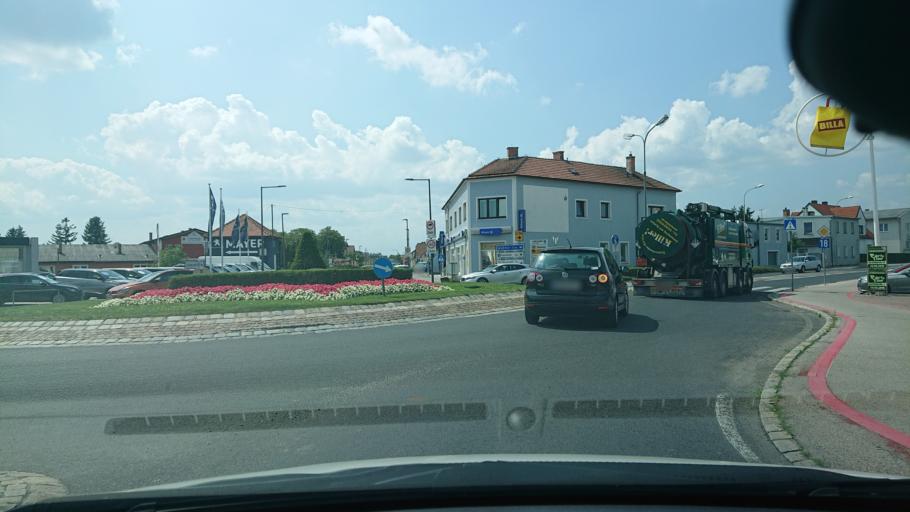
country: AT
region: Lower Austria
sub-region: Politischer Bezirk Baden
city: Leobersdorf
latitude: 47.9349
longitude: 16.2189
